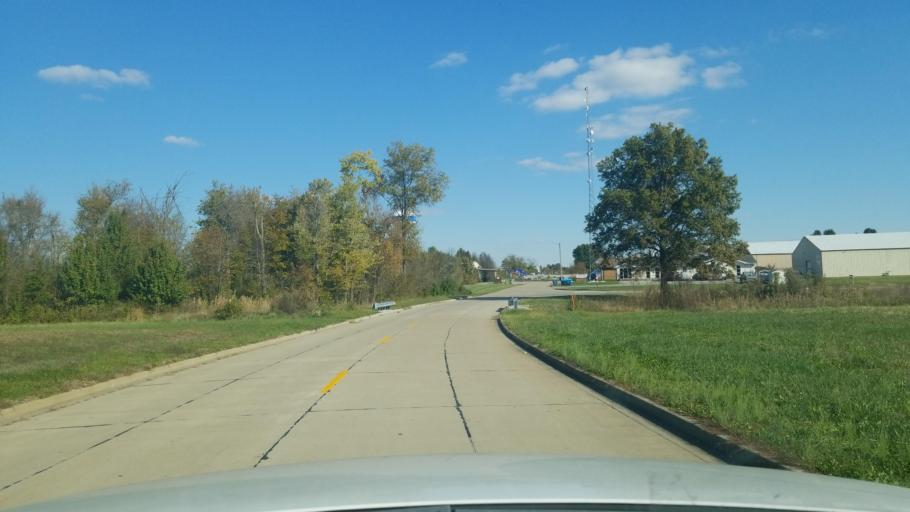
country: US
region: Illinois
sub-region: Williamson County
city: Energy
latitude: 37.7396
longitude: -88.9892
